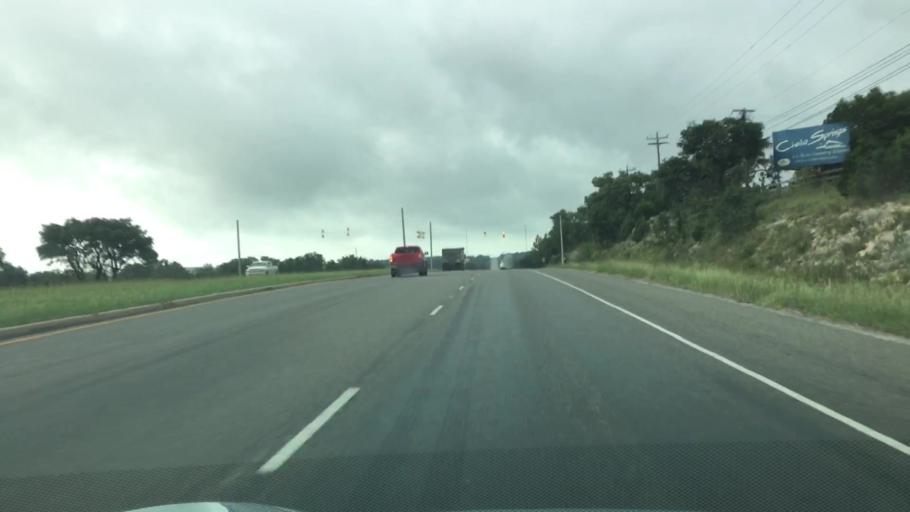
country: US
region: Texas
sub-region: Blanco County
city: Blanco
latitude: 30.0722
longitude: -98.4109
